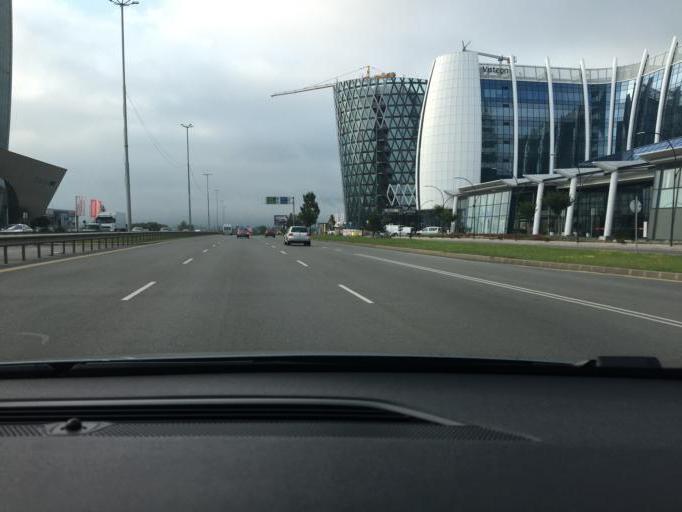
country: BG
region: Sofia-Capital
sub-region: Stolichna Obshtina
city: Sofia
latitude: 42.6474
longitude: 23.3961
